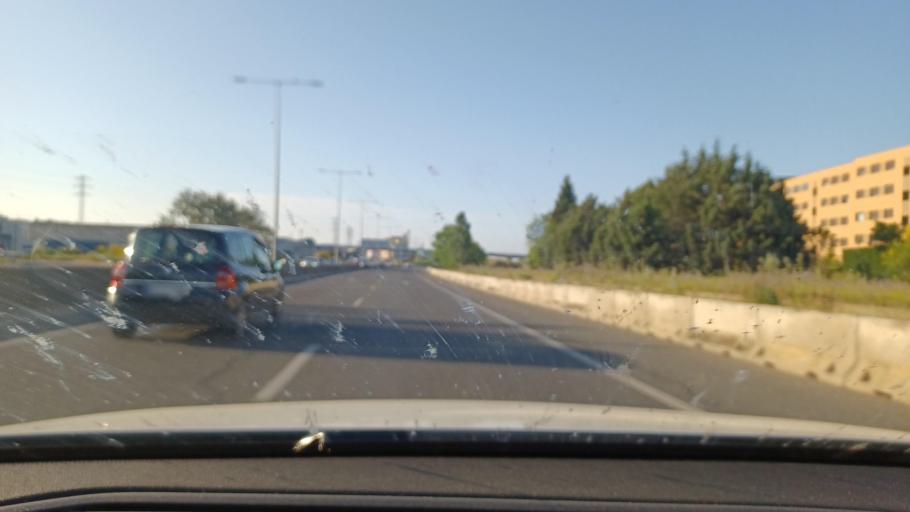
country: ES
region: Castille and Leon
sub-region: Provincia de Valladolid
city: Cisterniga
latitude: 41.6175
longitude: -4.7149
